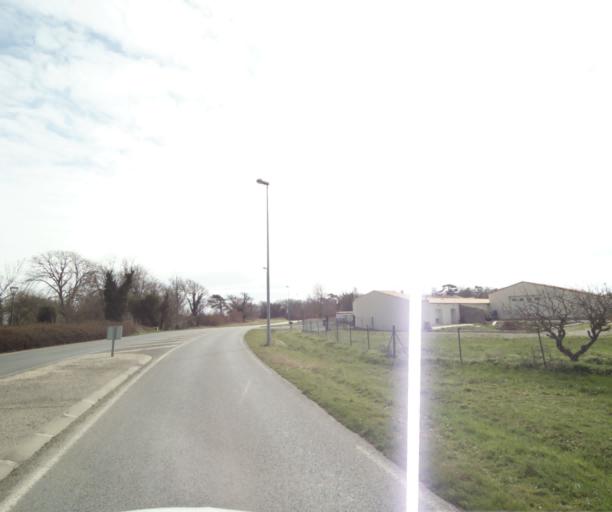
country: FR
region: Poitou-Charentes
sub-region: Departement de la Charente-Maritime
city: Lagord
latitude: 46.1844
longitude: -1.1748
